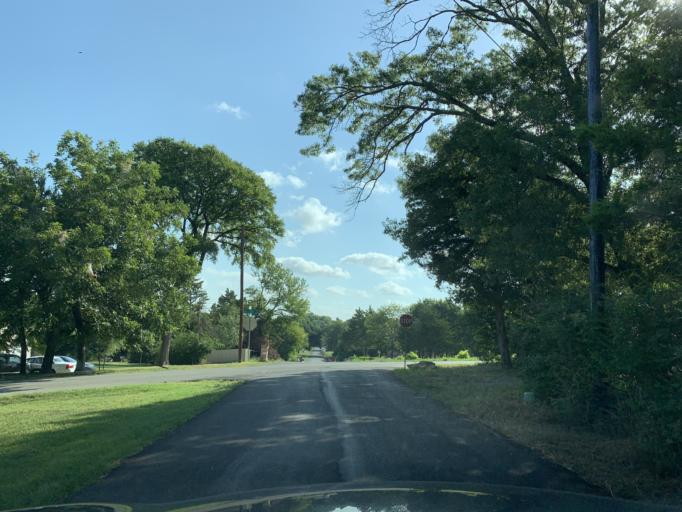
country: US
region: Texas
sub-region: Dallas County
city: Hutchins
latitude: 32.6754
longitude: -96.7811
